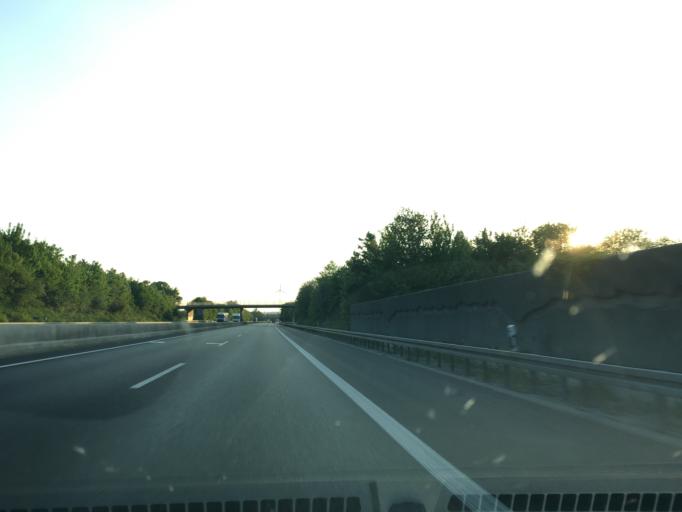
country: DE
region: North Rhine-Westphalia
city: Enger
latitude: 52.1932
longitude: 8.5213
